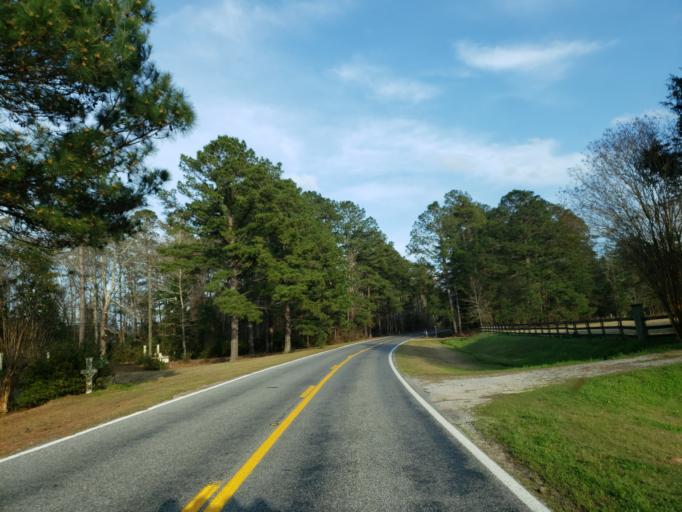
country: US
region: Mississippi
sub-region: Clarke County
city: Stonewall
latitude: 32.1776
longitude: -88.7995
